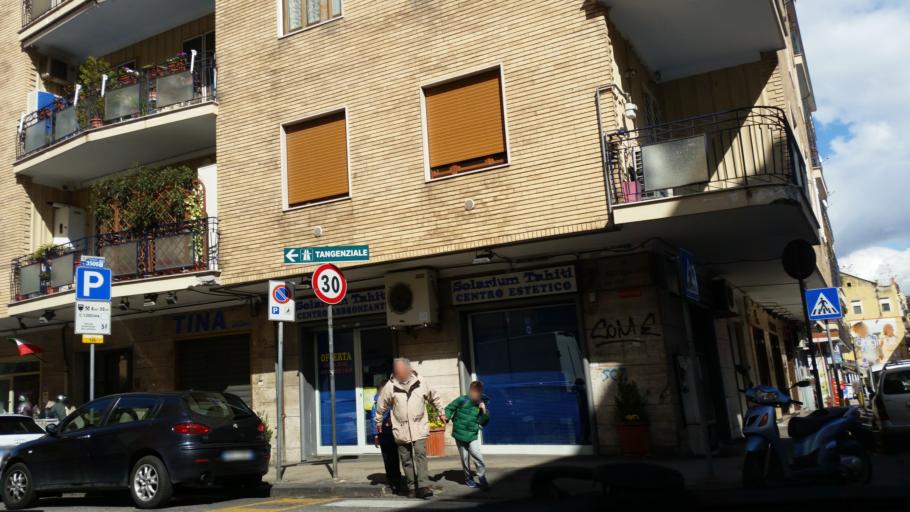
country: IT
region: Campania
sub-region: Provincia di Napoli
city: Napoli
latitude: 40.8419
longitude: 14.2220
